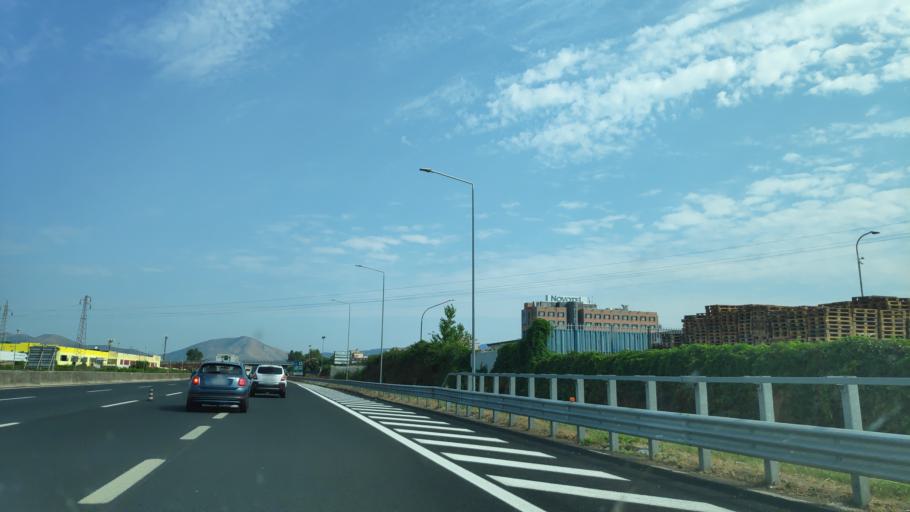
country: IT
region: Campania
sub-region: Provincia di Caserta
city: Capodrise
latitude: 41.0399
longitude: 14.3227
